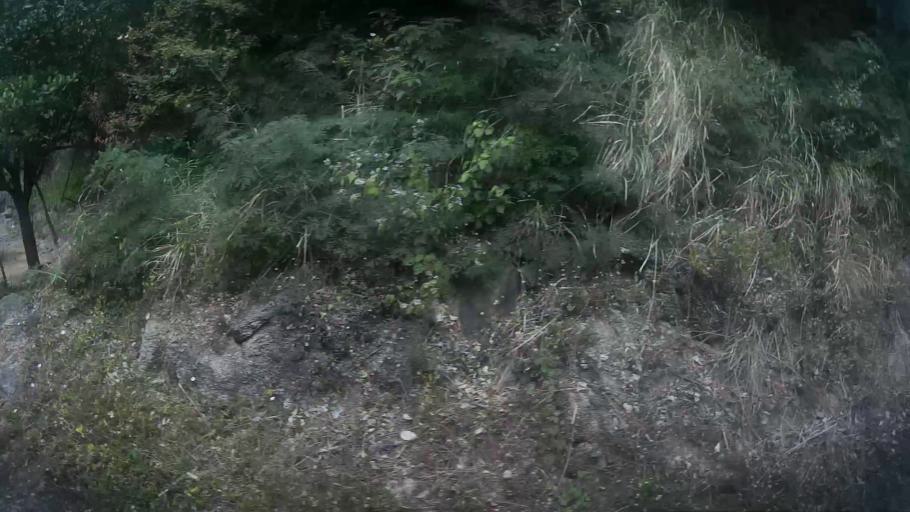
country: VN
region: Khanh Hoa
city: Van Gia
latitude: 12.8420
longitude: 109.3865
